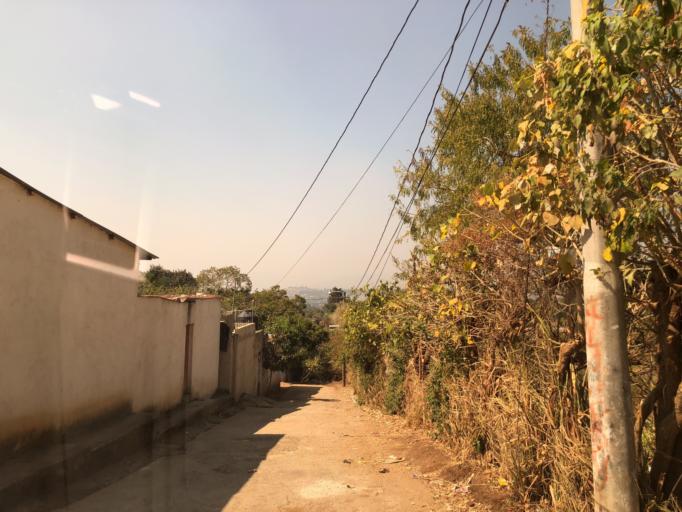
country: GT
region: Guatemala
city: Santa Catarina Pinula
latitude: 14.5369
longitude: -90.5098
